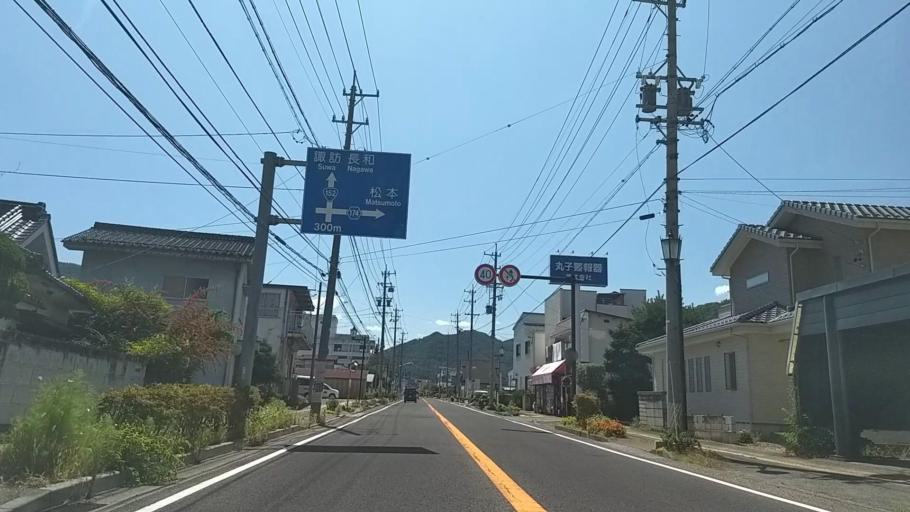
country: JP
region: Nagano
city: Kamimaruko
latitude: 36.3261
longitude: 138.2700
